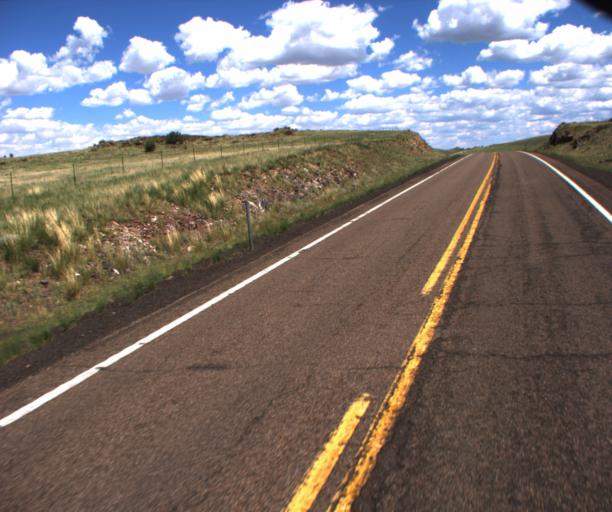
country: US
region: Arizona
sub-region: Apache County
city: Springerville
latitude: 34.2134
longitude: -109.4511
